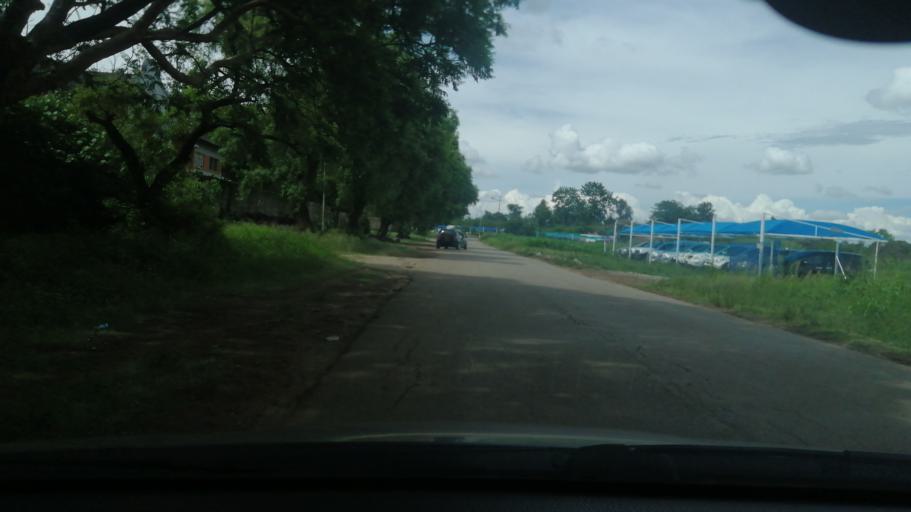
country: ZW
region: Harare
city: Harare
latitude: -17.8167
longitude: 31.0708
